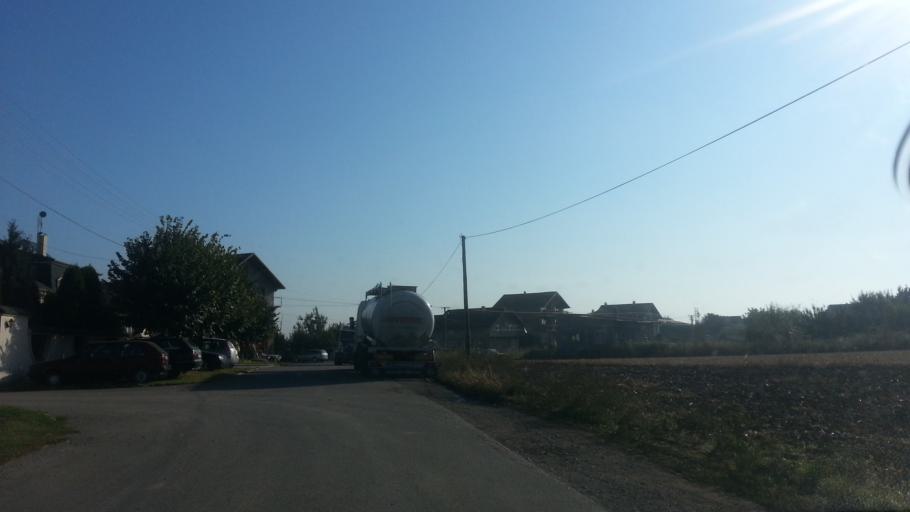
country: RS
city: Stari Banovci
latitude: 44.9866
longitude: 20.2651
